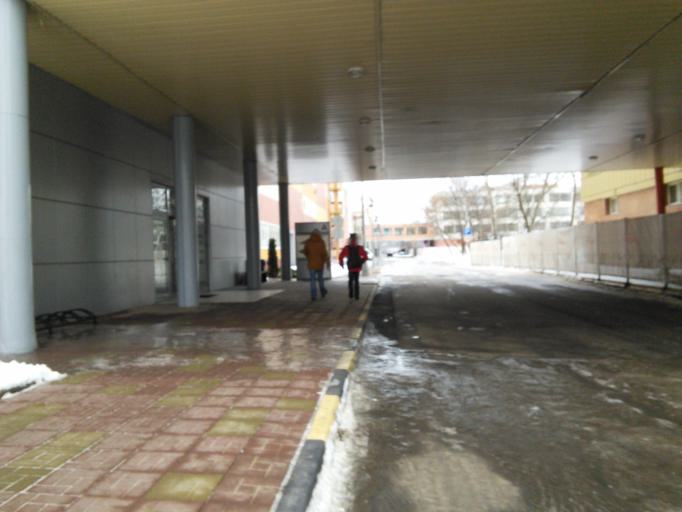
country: RU
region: Moscow
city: Tekstil'shchiki
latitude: 55.7085
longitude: 37.7251
